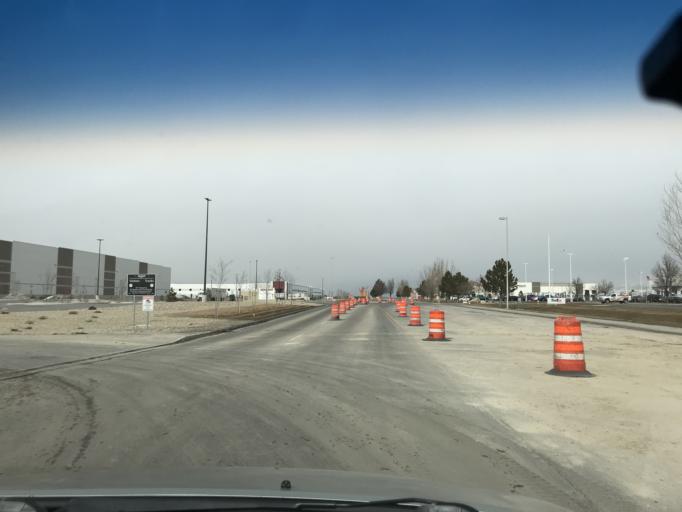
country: US
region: Utah
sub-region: Salt Lake County
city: West Valley City
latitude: 40.7841
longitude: -112.0251
